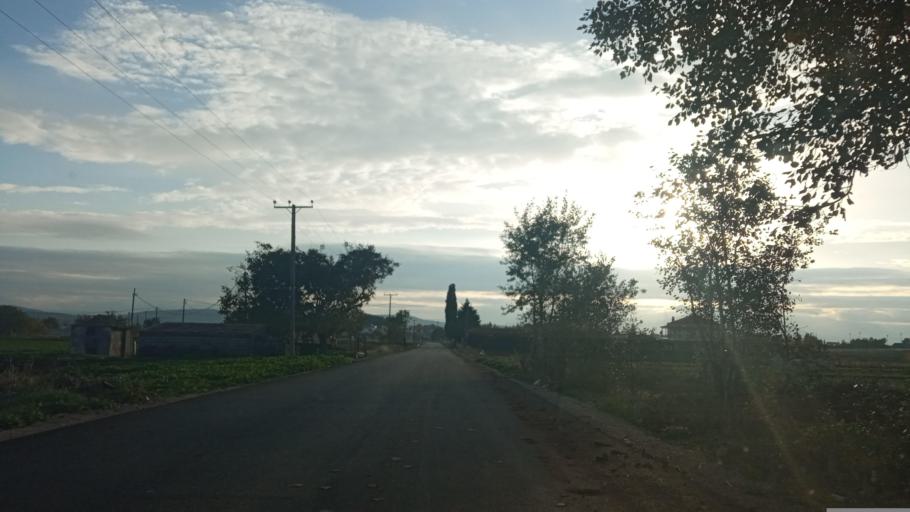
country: GR
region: Central Greece
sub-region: Nomos Evvoias
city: Psachna
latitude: 38.5908
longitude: 23.7193
